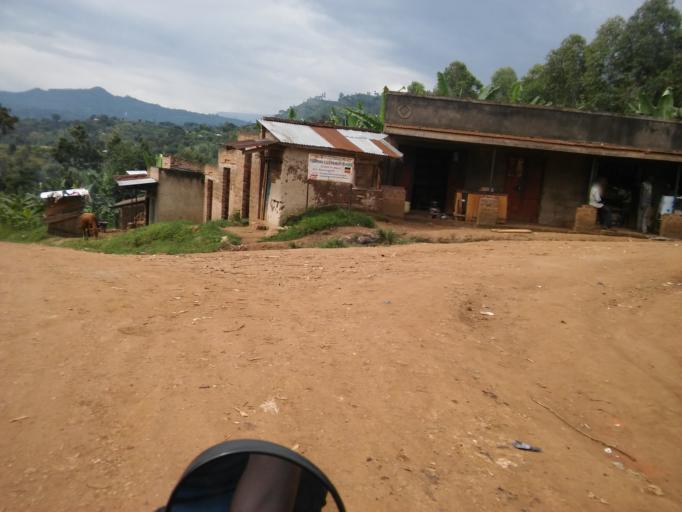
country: UG
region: Eastern Region
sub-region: Manafwa District
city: Manafwa
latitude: 0.9080
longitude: 34.3598
